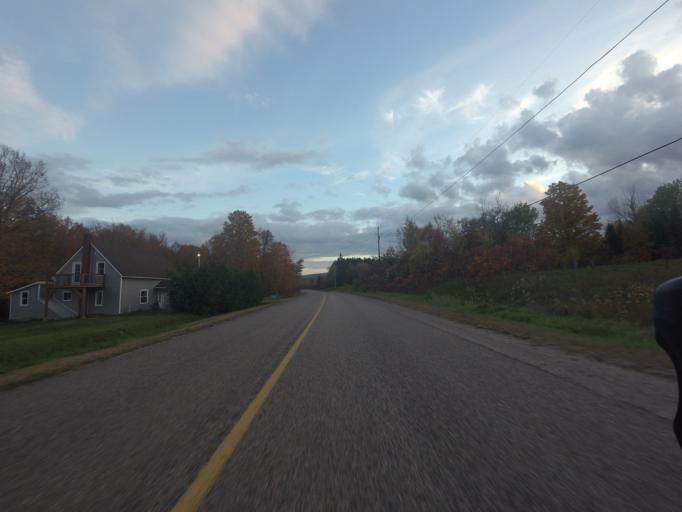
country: CA
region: Ontario
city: Renfrew
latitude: 45.3958
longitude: -76.9503
